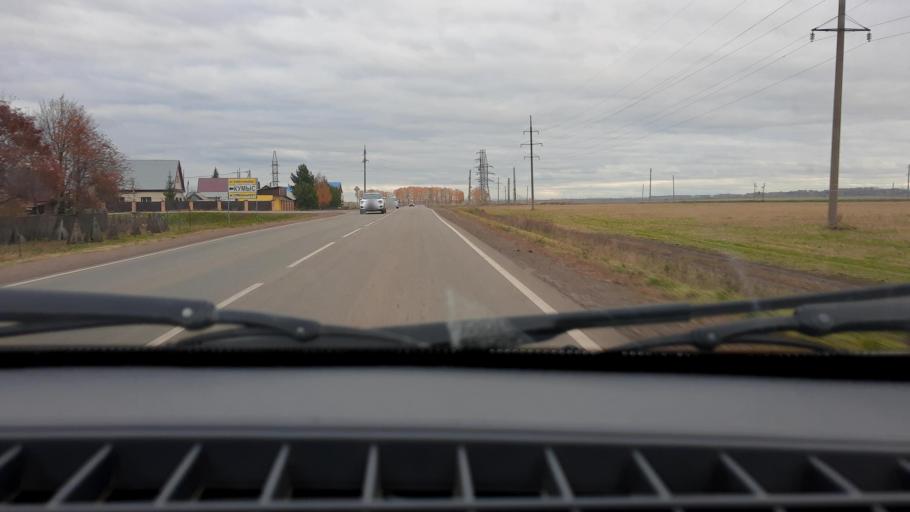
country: RU
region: Bashkortostan
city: Kabakovo
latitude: 54.5474
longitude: 56.0347
